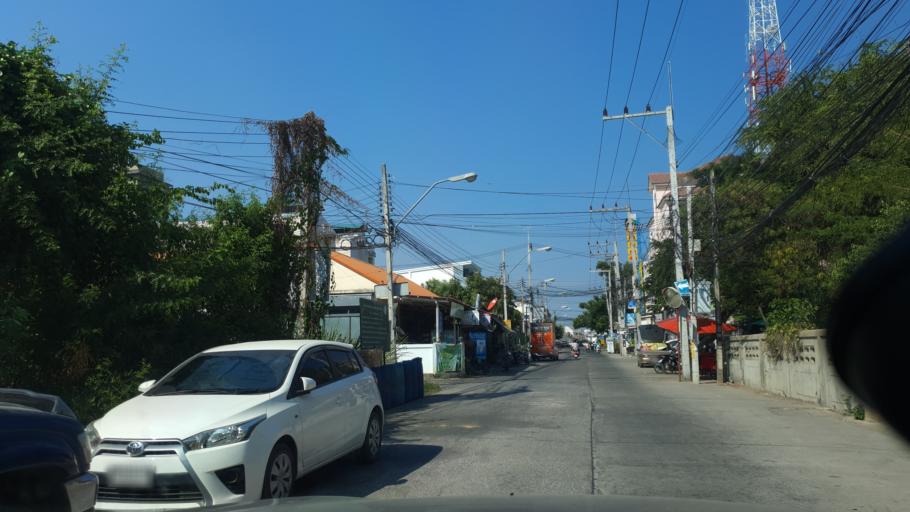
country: TH
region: Prachuap Khiri Khan
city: Hua Hin
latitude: 12.5551
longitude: 99.9526
